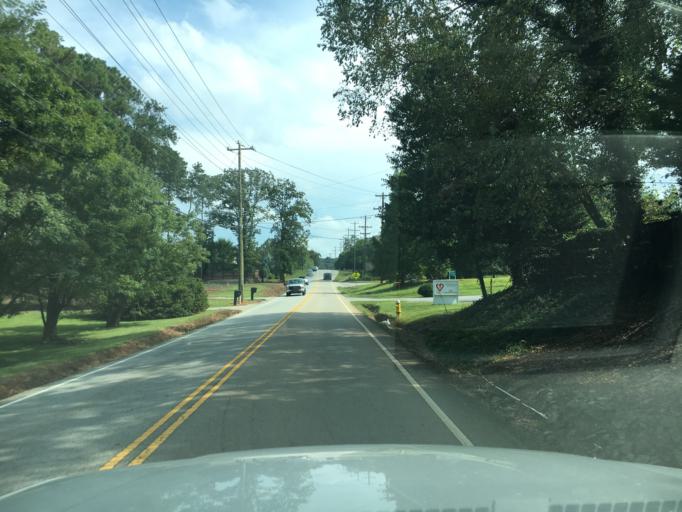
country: US
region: South Carolina
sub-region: Greenville County
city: Wade Hampton
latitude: 34.8491
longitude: -82.3145
